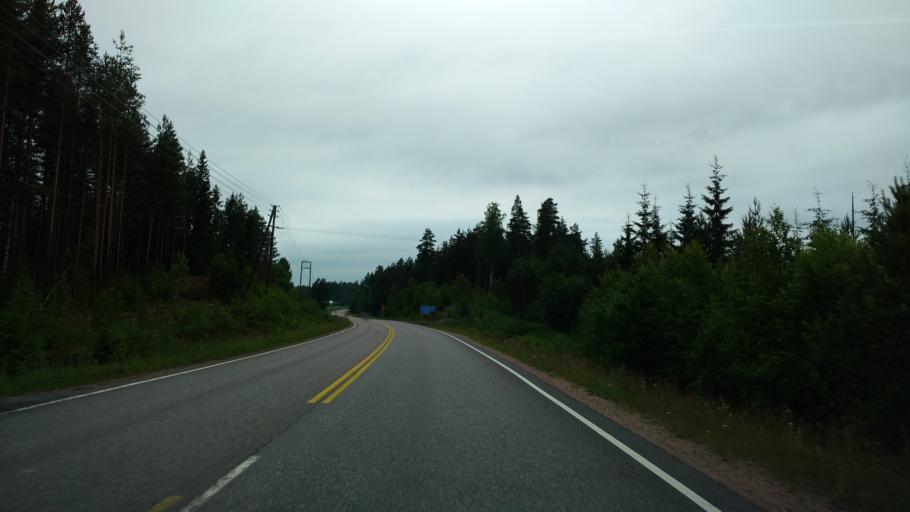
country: FI
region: Varsinais-Suomi
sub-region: Salo
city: Kiikala
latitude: 60.4258
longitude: 23.5934
